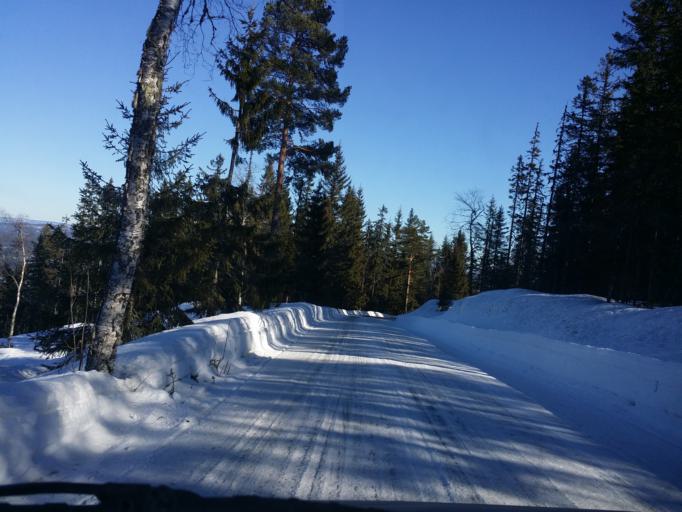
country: NO
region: Buskerud
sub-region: Ringerike
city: Honefoss
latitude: 60.4022
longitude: 10.0221
